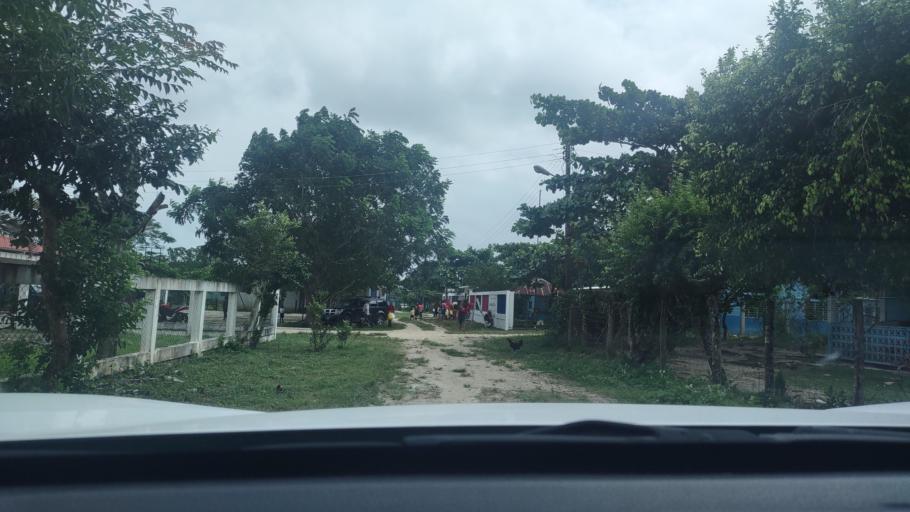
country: MX
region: Veracruz
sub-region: Moloacan
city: Cuichapa
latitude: 17.8983
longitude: -94.2995
